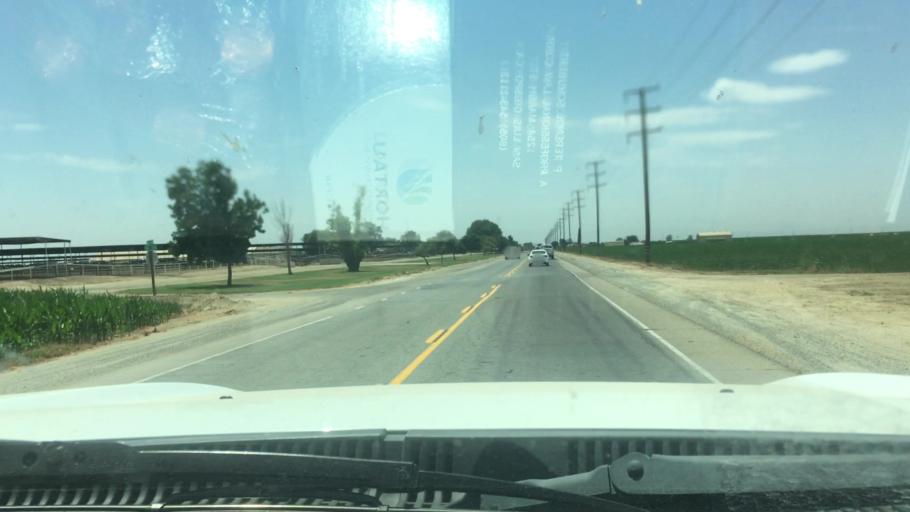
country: US
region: California
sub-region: Tulare County
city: Tipton
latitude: 36.0657
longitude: -119.2855
